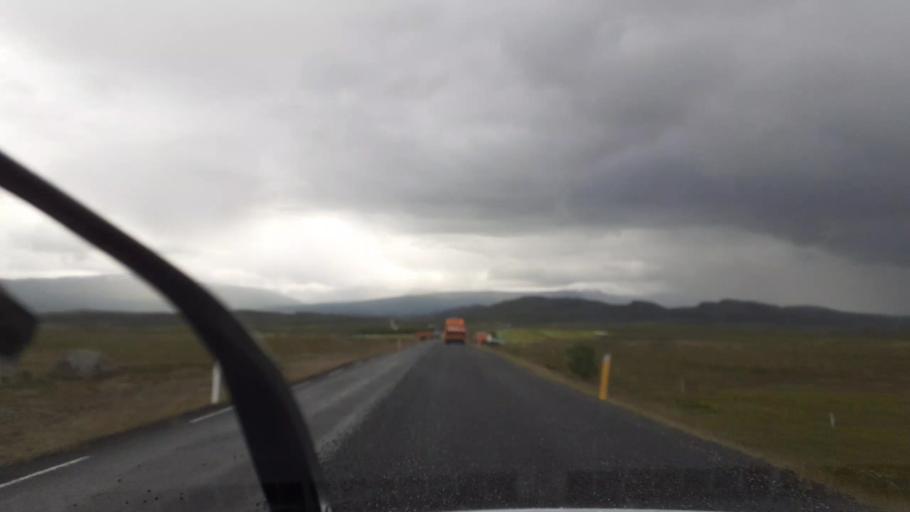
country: IS
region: East
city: Egilsstadir
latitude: 65.3453
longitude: -14.4965
